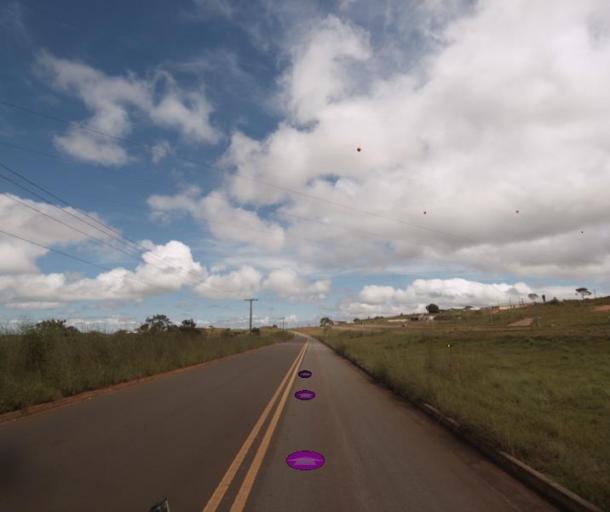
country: BR
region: Federal District
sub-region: Brasilia
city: Brasilia
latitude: -15.7407
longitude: -48.3096
